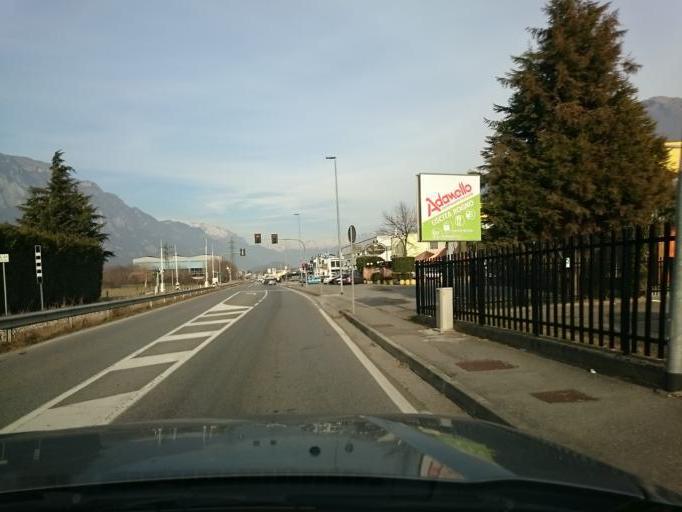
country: IT
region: Lombardy
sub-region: Provincia di Brescia
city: Artogne
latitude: 45.8603
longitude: 10.1608
